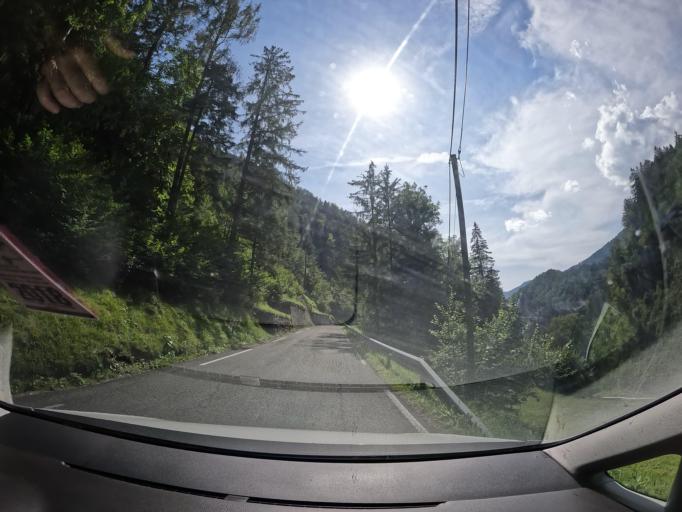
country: AT
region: Carinthia
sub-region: Politischer Bezirk Klagenfurt Land
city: Ludmannsdorf
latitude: 46.5138
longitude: 14.0993
